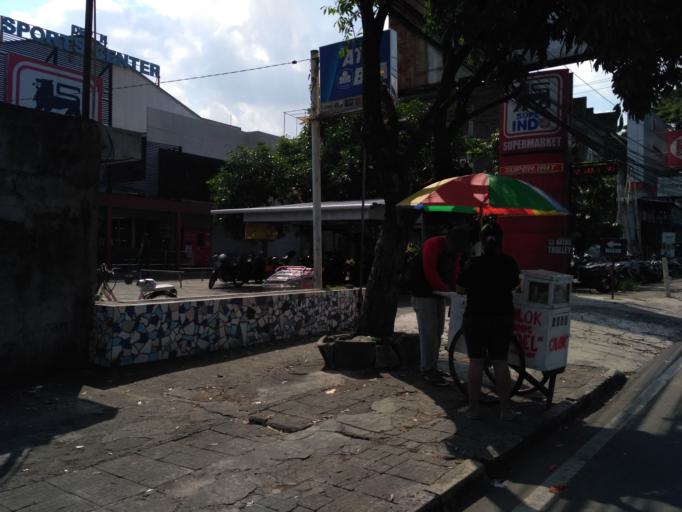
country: ID
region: Daerah Istimewa Yogyakarta
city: Depok
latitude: -7.7732
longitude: 110.4091
